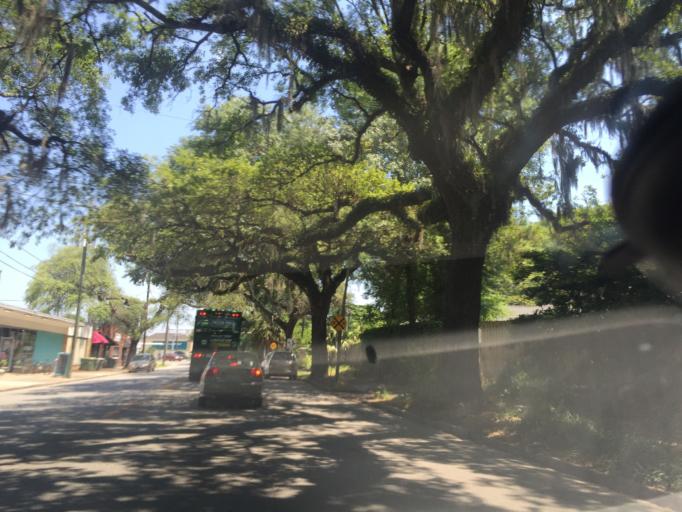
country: US
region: Georgia
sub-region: Chatham County
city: Savannah
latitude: 32.0512
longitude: -81.1026
